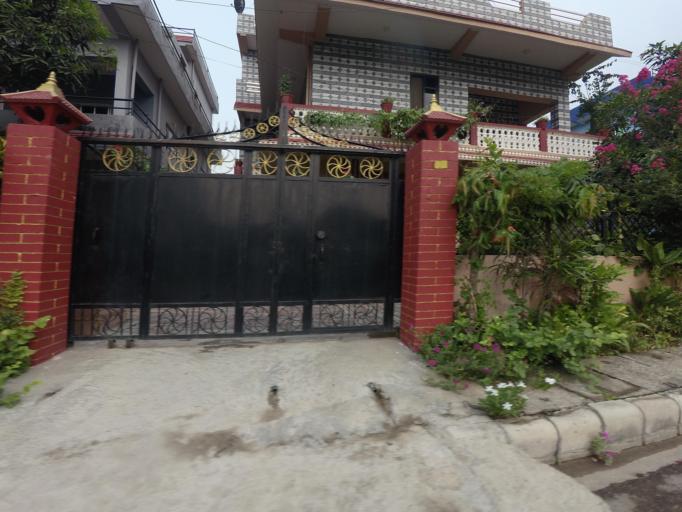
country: NP
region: Western Region
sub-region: Lumbini Zone
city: Bhairahawa
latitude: 27.5201
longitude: 83.4452
